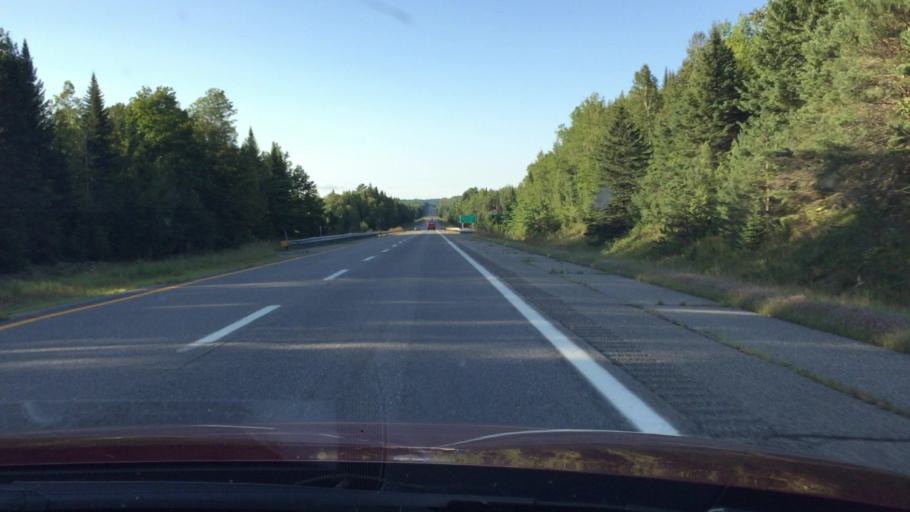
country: US
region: Maine
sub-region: Penobscot County
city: Patten
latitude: 45.8100
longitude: -68.4284
